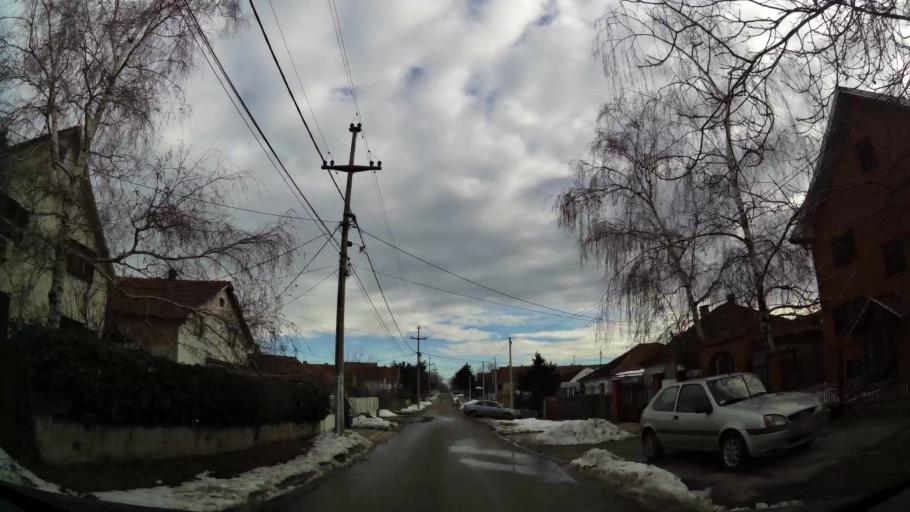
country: RS
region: Central Serbia
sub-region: Belgrade
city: Surcin
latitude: 44.8002
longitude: 20.2889
